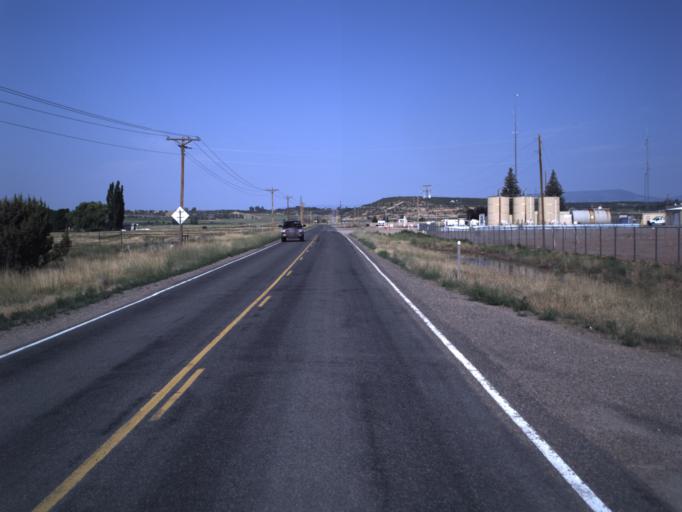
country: US
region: Utah
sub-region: Duchesne County
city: Duchesne
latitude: 40.3557
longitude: -110.3261
